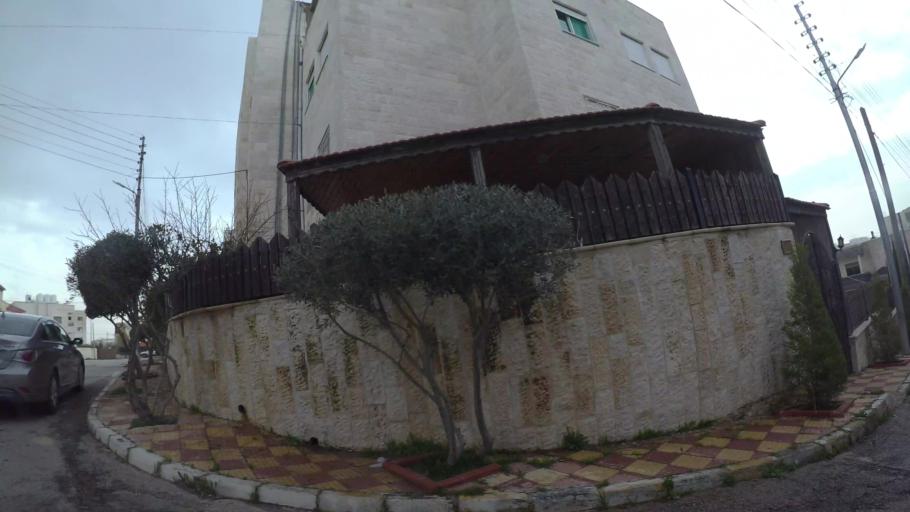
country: JO
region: Amman
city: Umm as Summaq
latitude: 31.9037
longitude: 35.8338
